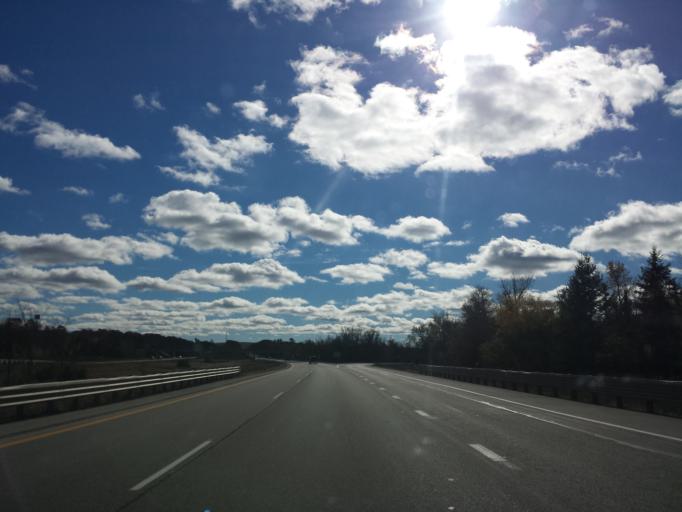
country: US
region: Michigan
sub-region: Cheboygan County
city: Indian River
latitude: 45.4061
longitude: -84.6073
